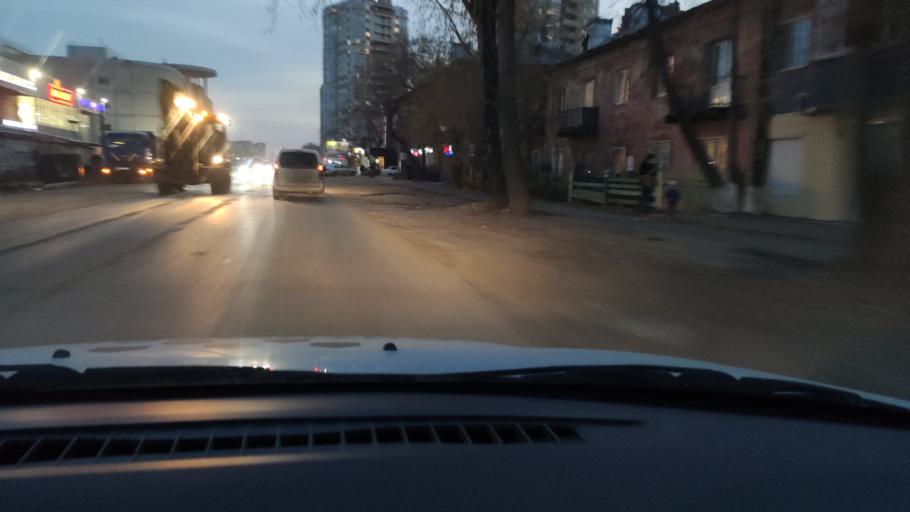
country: RU
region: Perm
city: Perm
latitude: 57.9725
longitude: 56.2067
